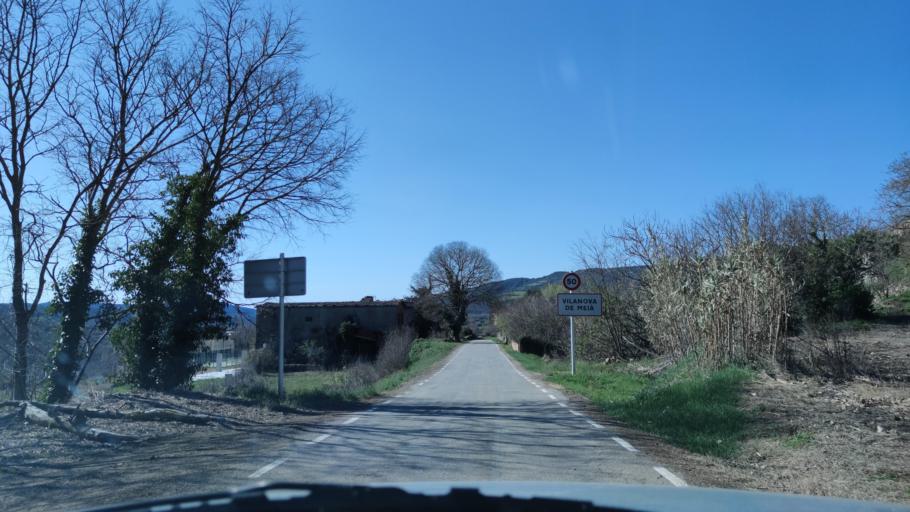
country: ES
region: Catalonia
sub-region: Provincia de Lleida
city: Artesa de Segre
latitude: 41.9974
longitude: 1.0257
